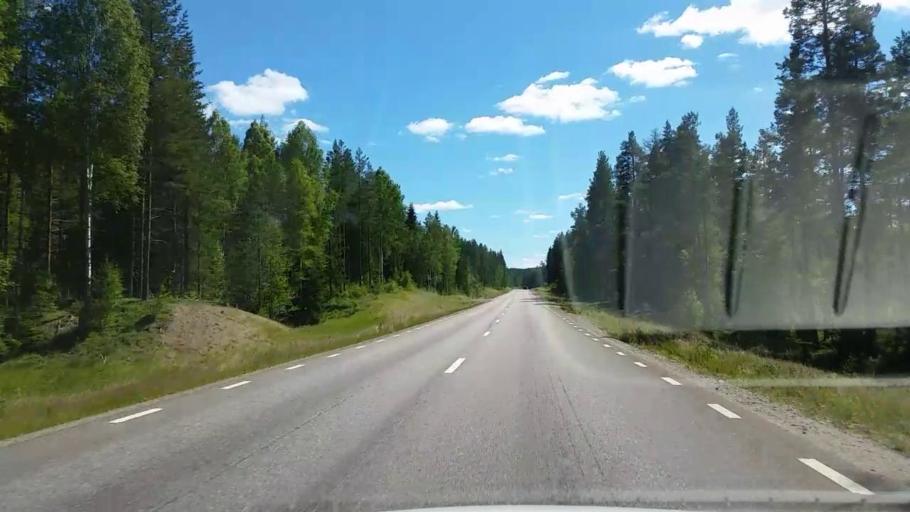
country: SE
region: Gaevleborg
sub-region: Ovanakers Kommun
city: Edsbyn
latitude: 61.1849
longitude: 15.8774
